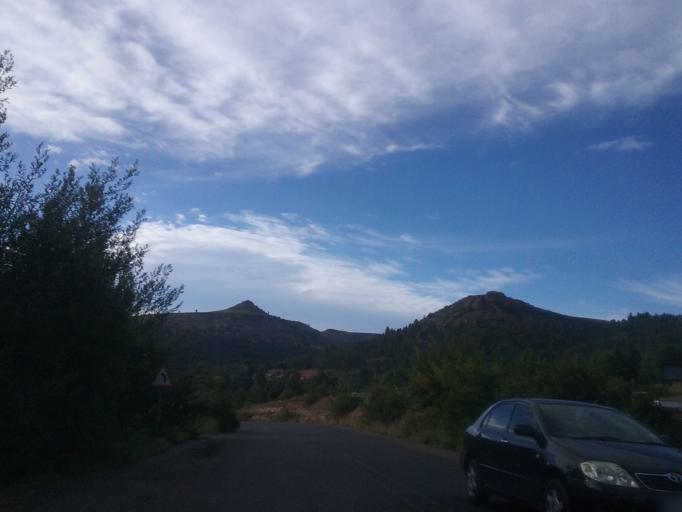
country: LS
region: Quthing
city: Quthing
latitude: -30.4018
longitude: 27.6751
